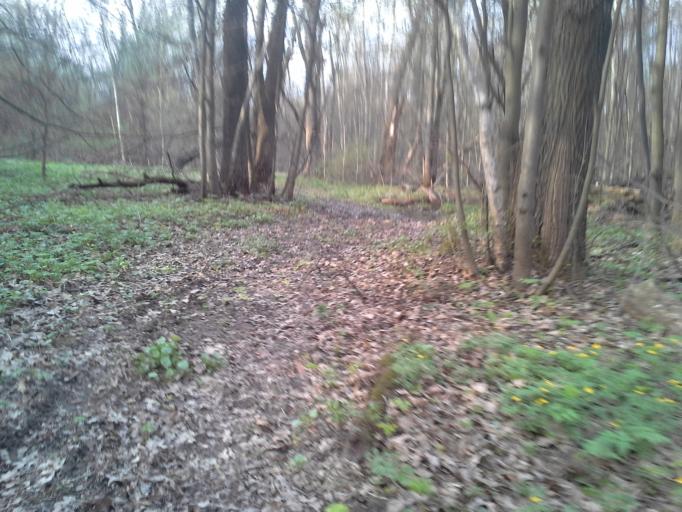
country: RU
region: Moskovskaya
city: Kommunarka
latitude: 55.5842
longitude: 37.5006
